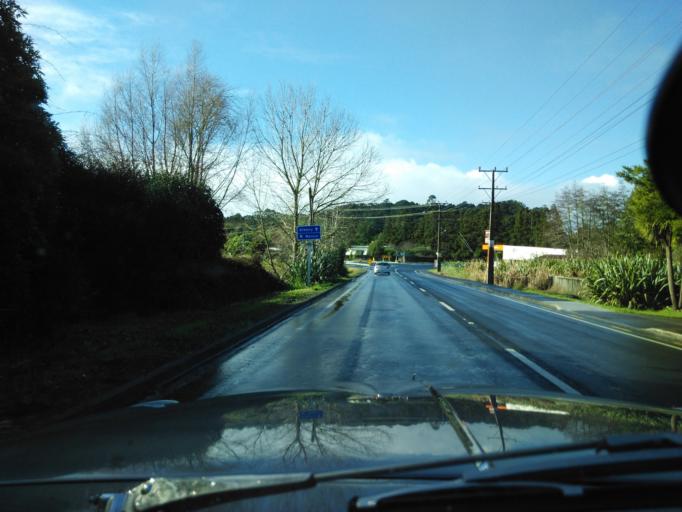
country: NZ
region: Auckland
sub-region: Auckland
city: Parakai
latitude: -36.6350
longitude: 174.5499
